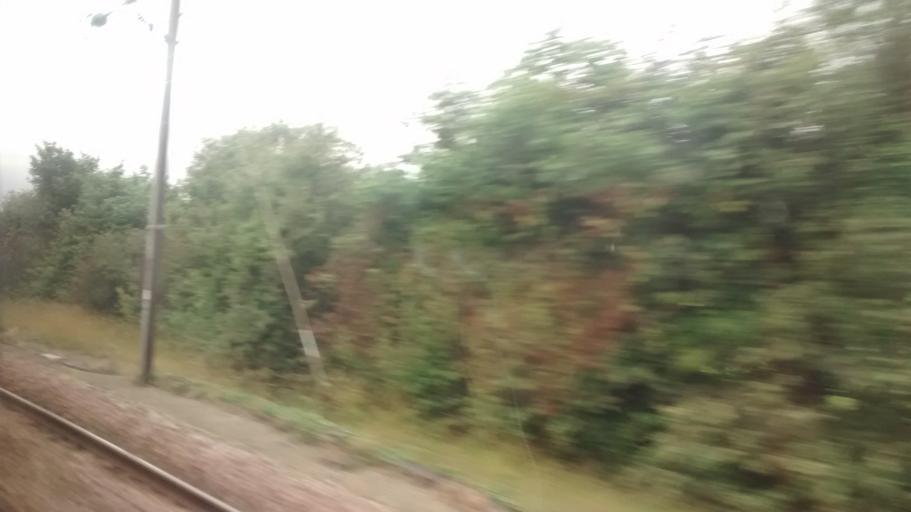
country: FR
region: Pays de la Loire
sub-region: Departement de la Mayenne
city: Argentre
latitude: 48.1262
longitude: -0.6517
